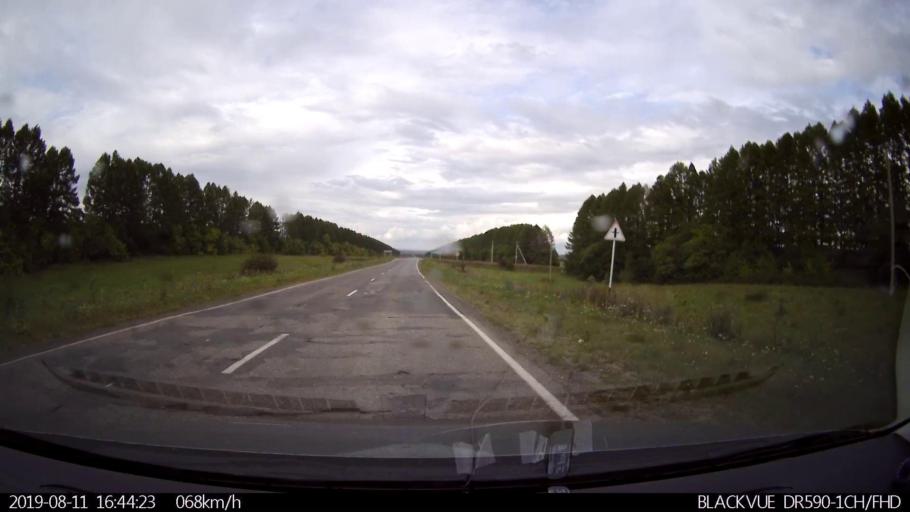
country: RU
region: Ulyanovsk
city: Mayna
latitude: 54.1784
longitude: 47.6795
